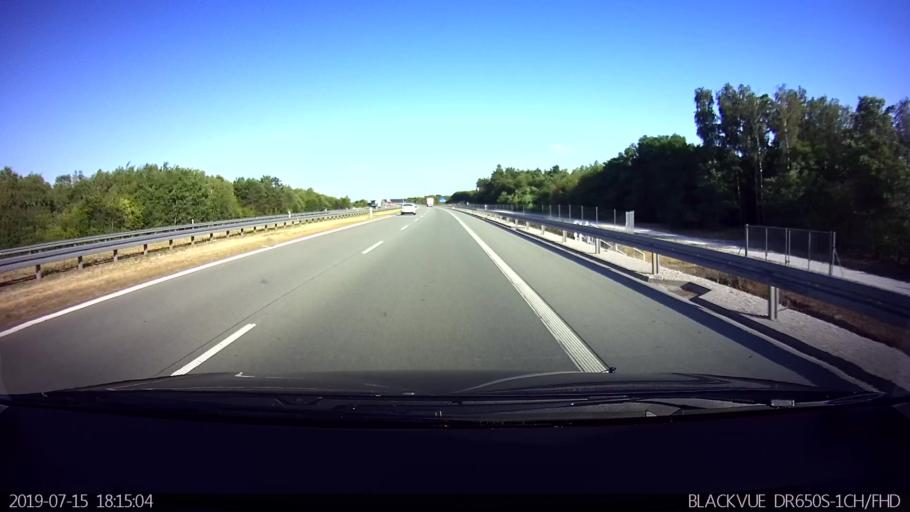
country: PL
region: Lodz Voivodeship
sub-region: Powiat zdunskowolski
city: Zdunska Wola
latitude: 51.5842
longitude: 18.9012
